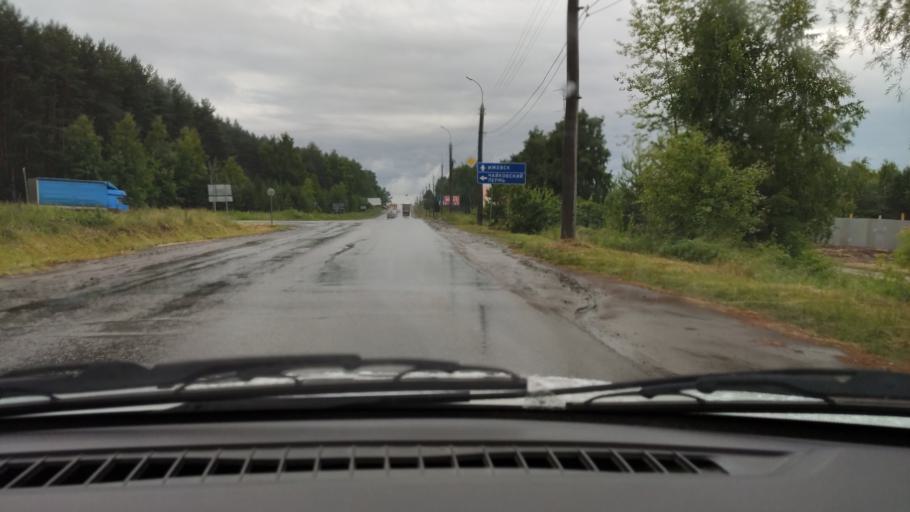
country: RU
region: Udmurtiya
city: Votkinsk
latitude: 57.0340
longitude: 53.9402
